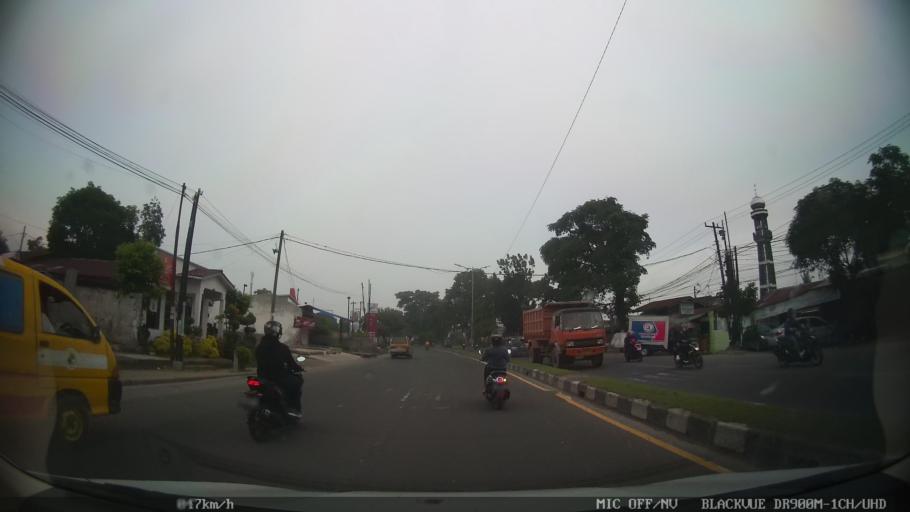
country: ID
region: North Sumatra
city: Deli Tua
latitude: 3.5334
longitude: 98.7233
